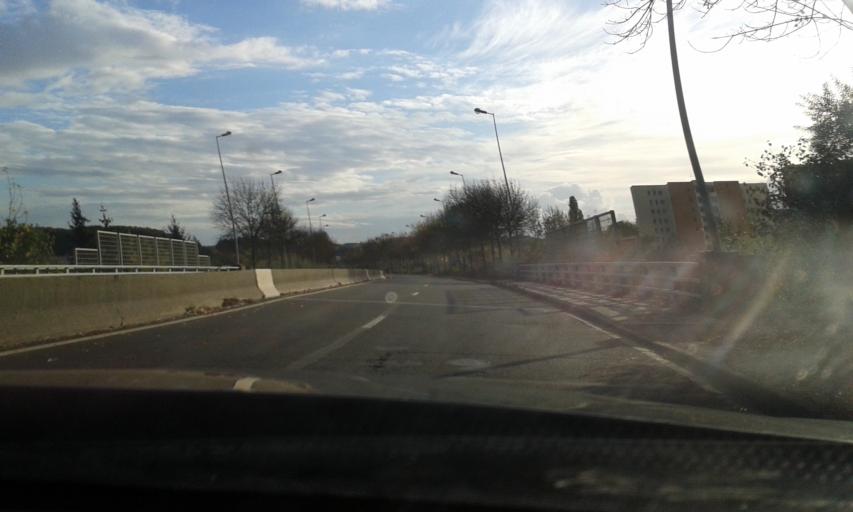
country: FR
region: Centre
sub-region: Departement d'Eure-et-Loir
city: Dreux
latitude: 48.7362
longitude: 1.3423
